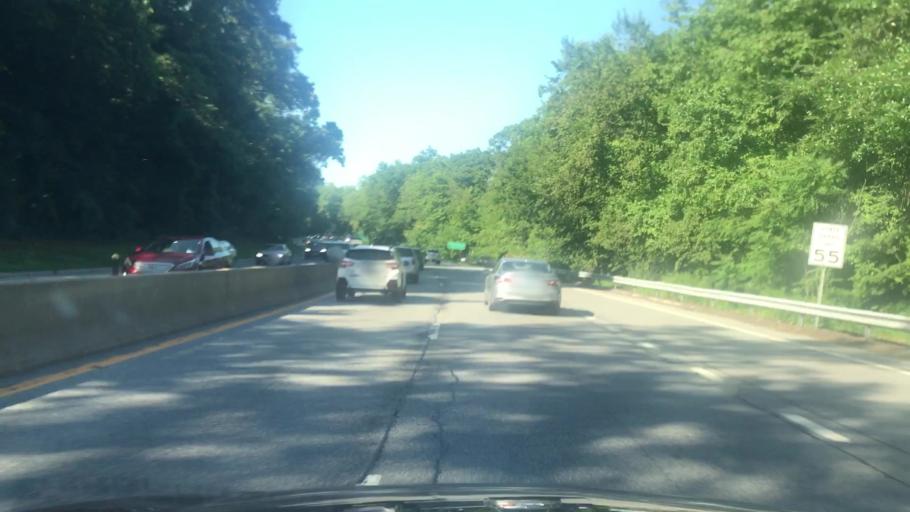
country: US
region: New York
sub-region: Westchester County
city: Scarsdale
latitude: 40.9717
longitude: -73.7665
